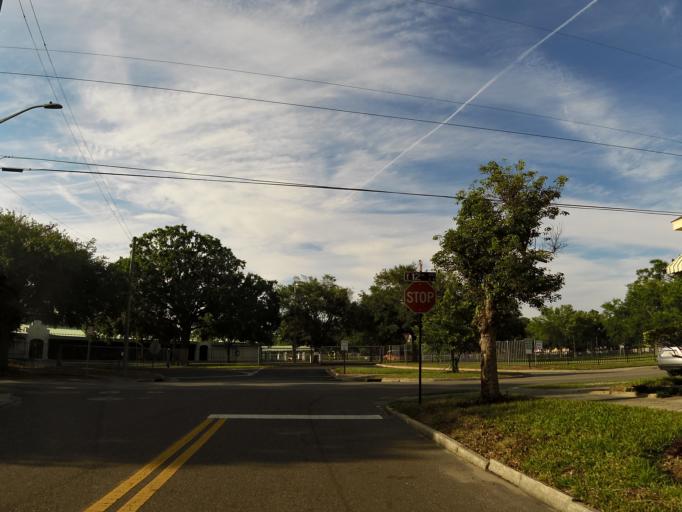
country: US
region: Florida
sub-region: Duval County
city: Jacksonville
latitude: 30.3506
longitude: -81.6552
